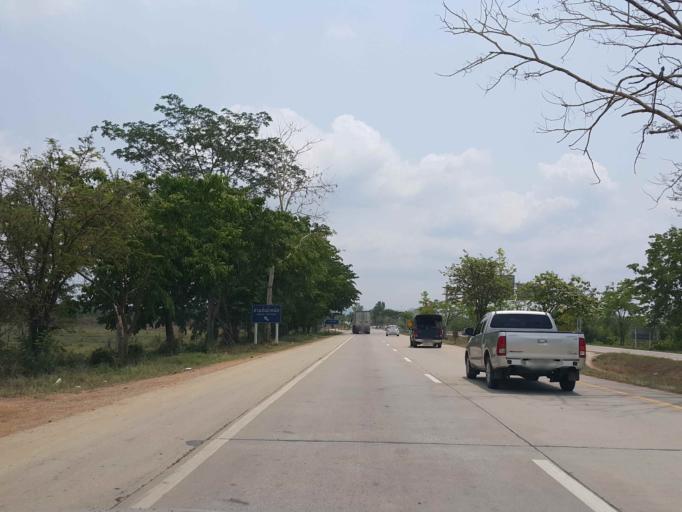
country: TH
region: Lampang
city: Ko Kha
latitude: 18.1880
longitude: 99.4074
